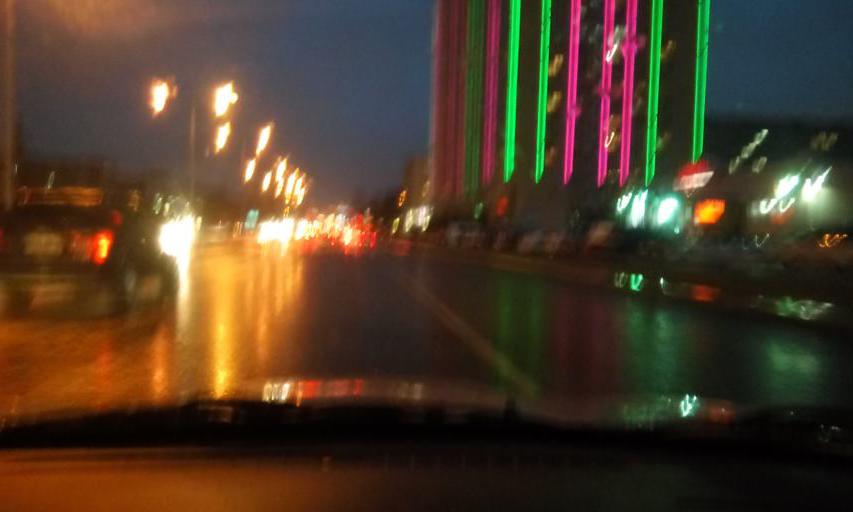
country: KZ
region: Astana Qalasy
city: Astana
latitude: 51.1749
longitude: 71.4033
